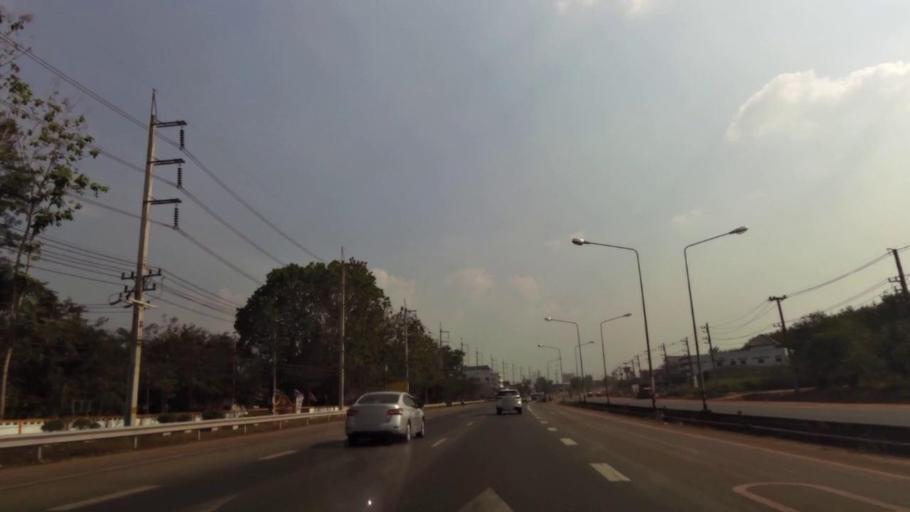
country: TH
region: Rayong
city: Wang Chan
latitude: 12.9439
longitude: 101.5185
